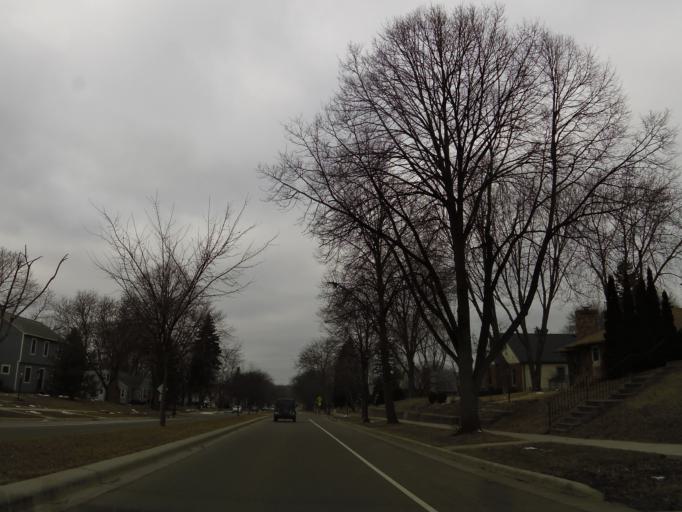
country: US
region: Minnesota
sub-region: Dakota County
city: Mendota Heights
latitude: 44.9126
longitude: -93.1802
